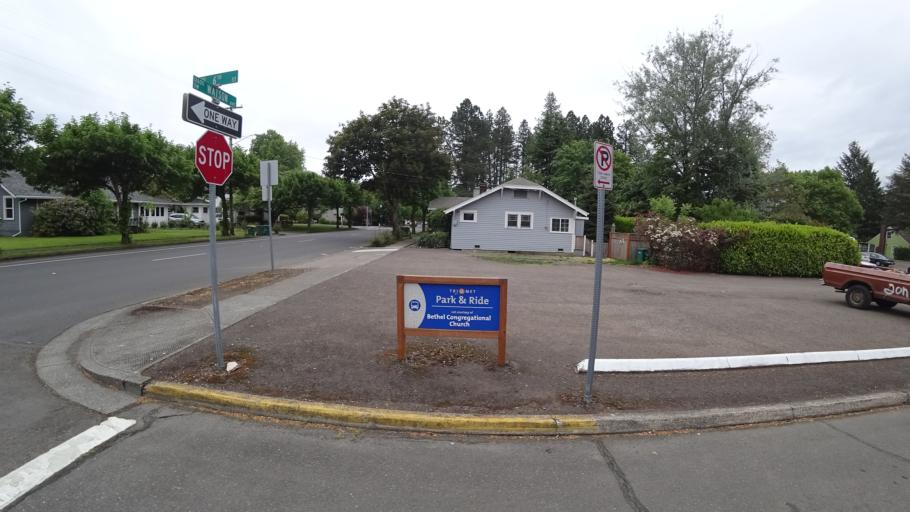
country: US
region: Oregon
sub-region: Washington County
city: Beaverton
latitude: 45.4829
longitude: -122.8068
